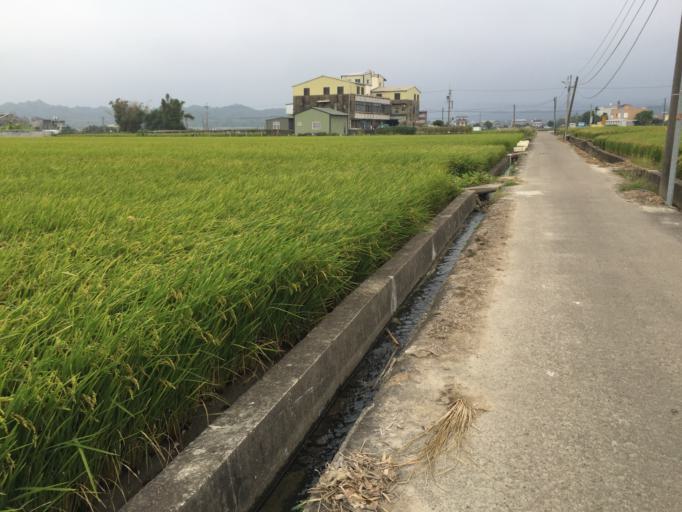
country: TW
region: Taiwan
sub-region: Miaoli
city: Miaoli
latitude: 24.5824
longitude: 120.8318
